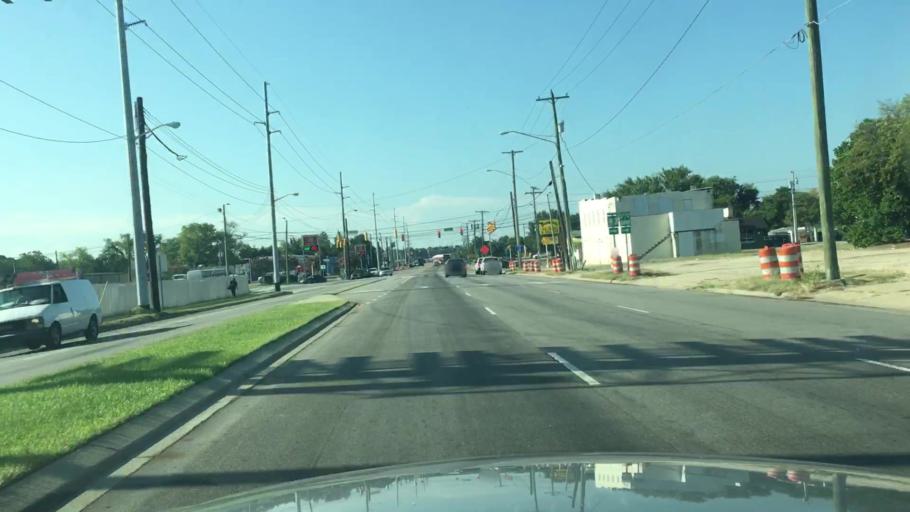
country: US
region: North Carolina
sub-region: Cumberland County
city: Fayetteville
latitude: 35.0492
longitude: -78.8650
